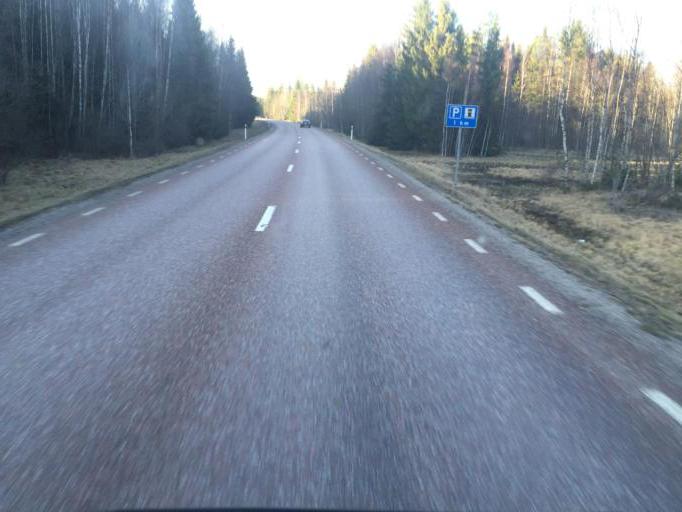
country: SE
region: Dalarna
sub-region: Gagnefs Kommun
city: Mockfjard
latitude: 60.4713
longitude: 14.7698
